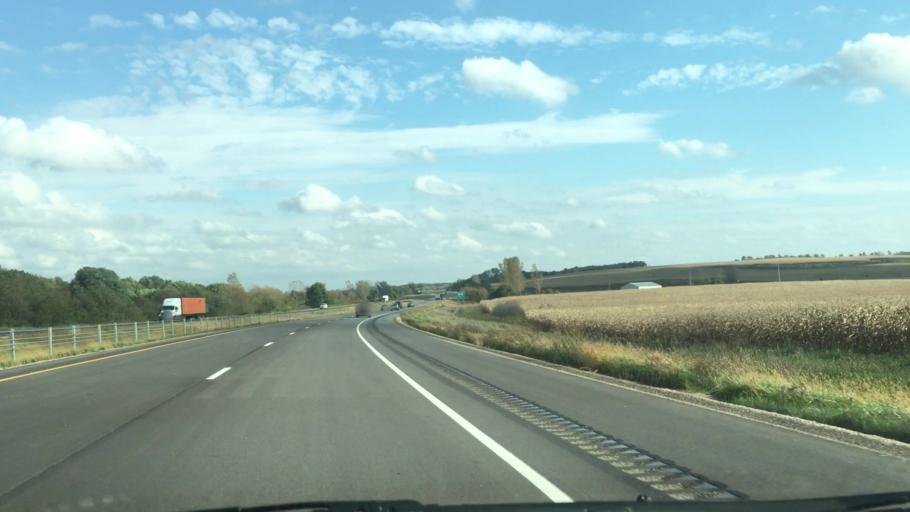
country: US
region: Minnesota
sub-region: Olmsted County
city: Rochester
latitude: 43.9704
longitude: -92.4022
